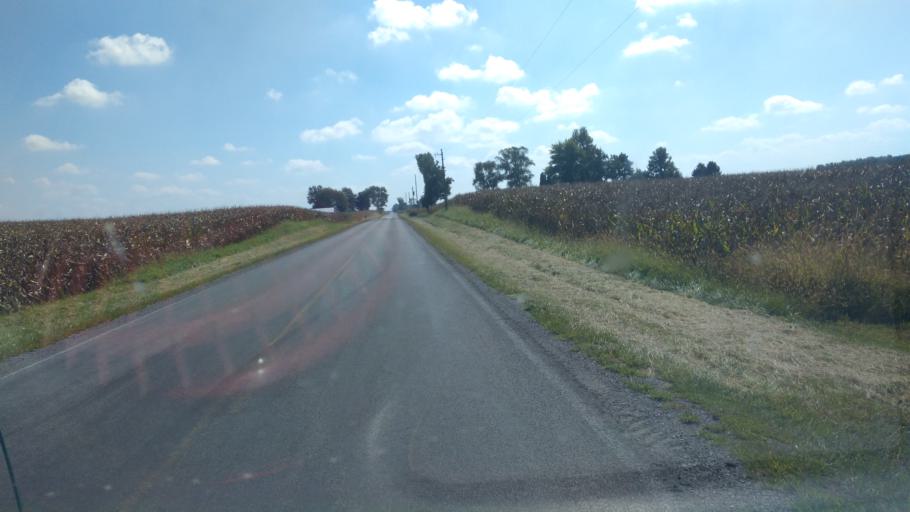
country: US
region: Ohio
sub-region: Hardin County
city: Ada
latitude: 40.7693
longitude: -83.7849
